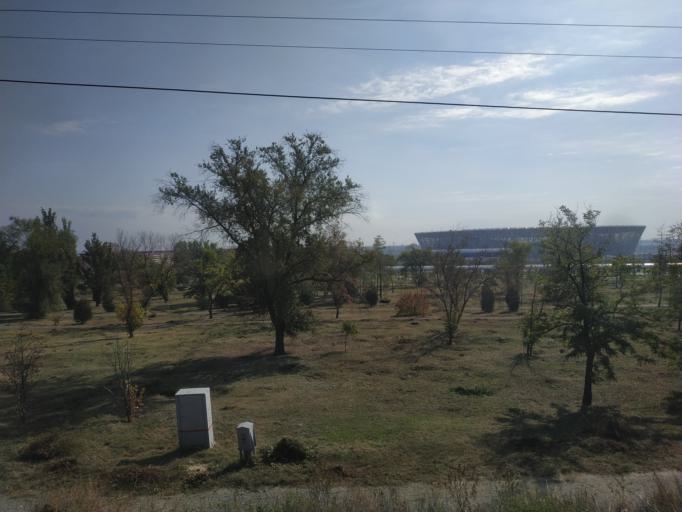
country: RU
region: Volgograd
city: Volgograd
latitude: 48.7389
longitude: 44.5415
